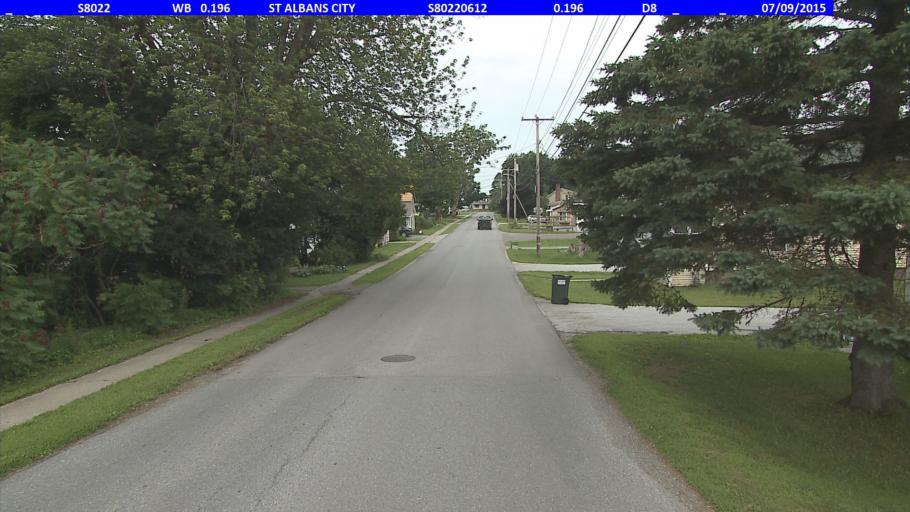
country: US
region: Vermont
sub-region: Franklin County
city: Saint Albans
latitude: 44.8036
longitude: -73.0917
